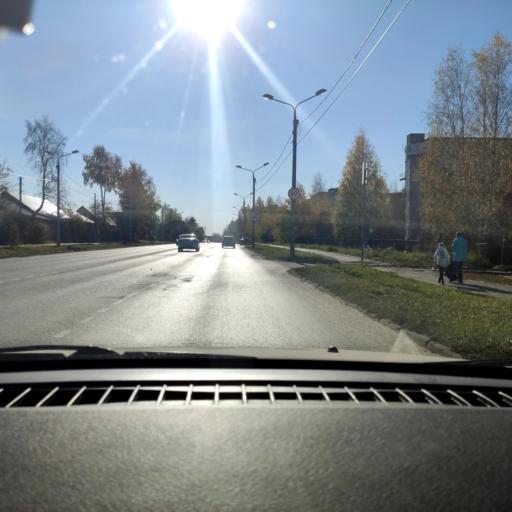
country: RU
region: Perm
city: Perm
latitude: 58.0583
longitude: 56.3585
